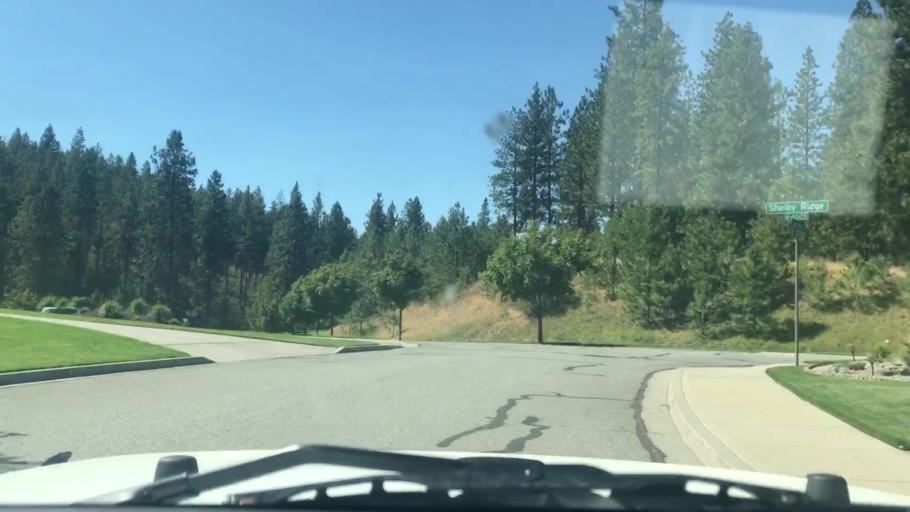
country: US
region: Washington
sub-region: Spokane County
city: Spokane
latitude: 47.5949
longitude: -117.4201
